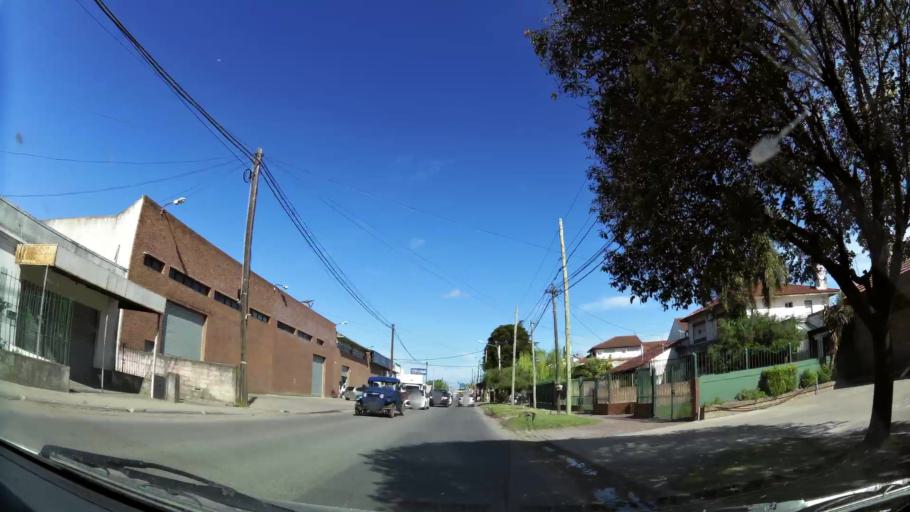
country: AR
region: Buenos Aires
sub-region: Partido de Quilmes
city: Quilmes
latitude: -34.8056
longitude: -58.2167
